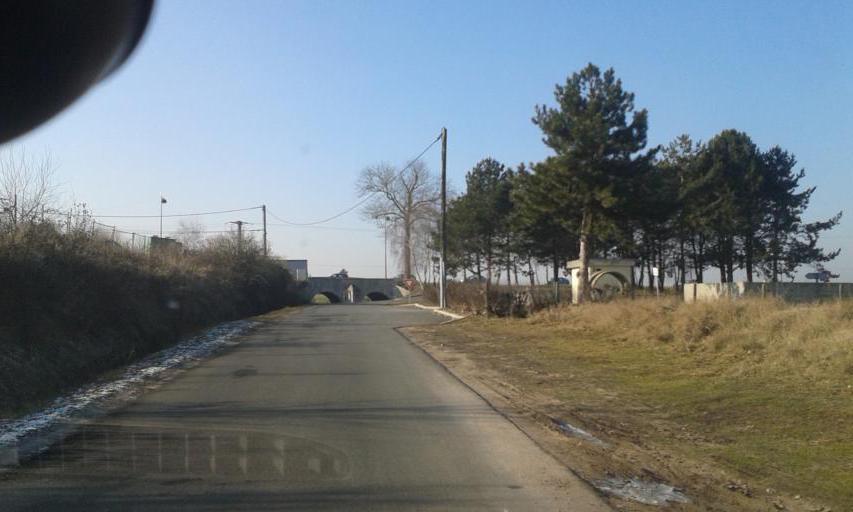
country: FR
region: Centre
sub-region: Departement du Loiret
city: Chevilly
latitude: 47.9902
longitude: 1.8837
